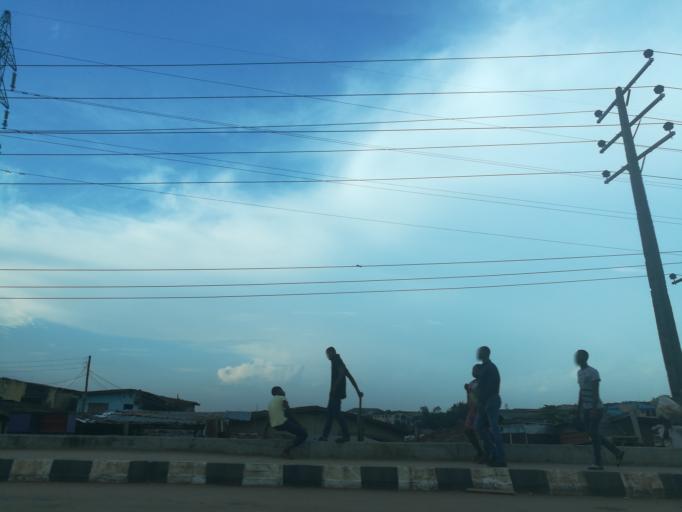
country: NG
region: Lagos
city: Ikorodu
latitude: 6.6258
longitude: 3.4863
